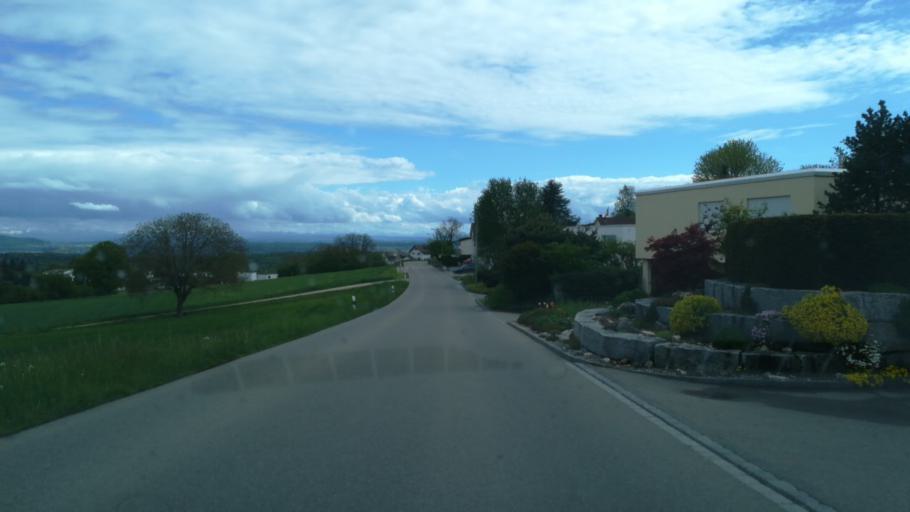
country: CH
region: Schaffhausen
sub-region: Bezirk Reiat
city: Stetten
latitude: 47.7443
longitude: 8.6627
